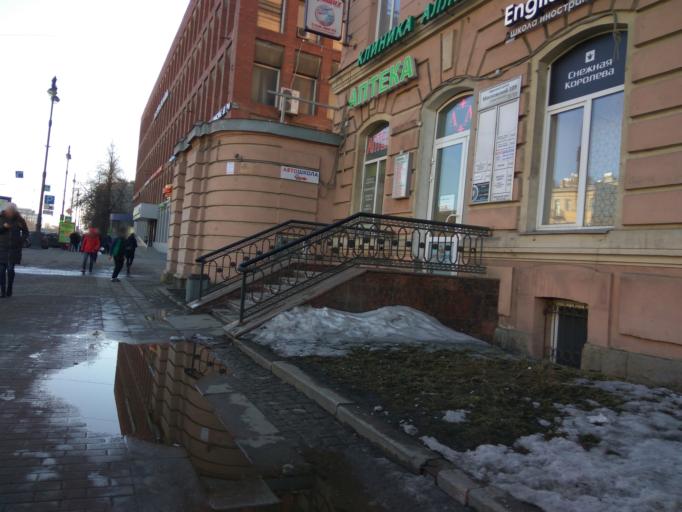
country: RU
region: St.-Petersburg
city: Admiralteisky
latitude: 59.8895
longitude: 30.3191
